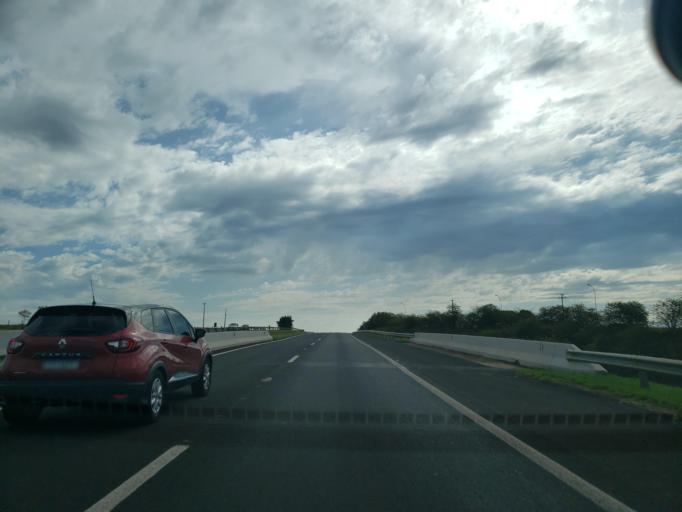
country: BR
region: Sao Paulo
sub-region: Cafelandia
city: Cafelandia
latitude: -21.8066
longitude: -49.6321
